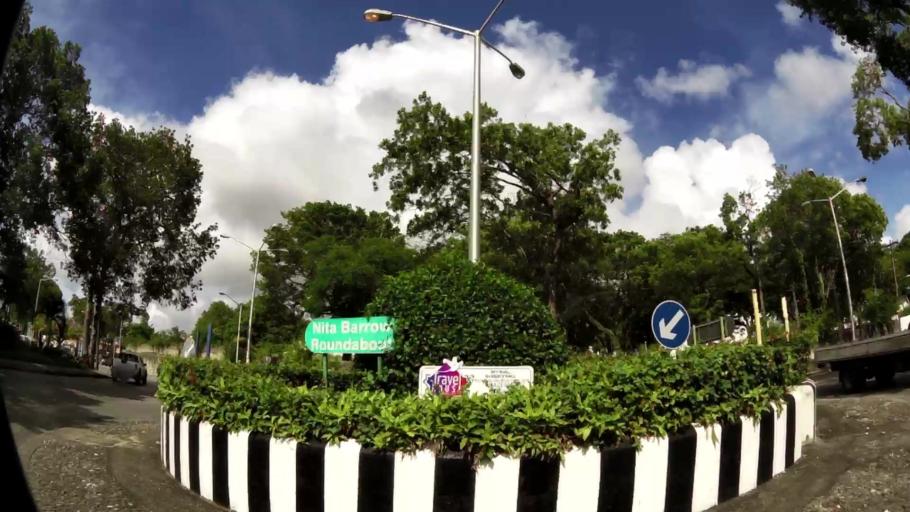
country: BB
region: Saint Michael
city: Bridgetown
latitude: 13.1006
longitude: -59.6009
